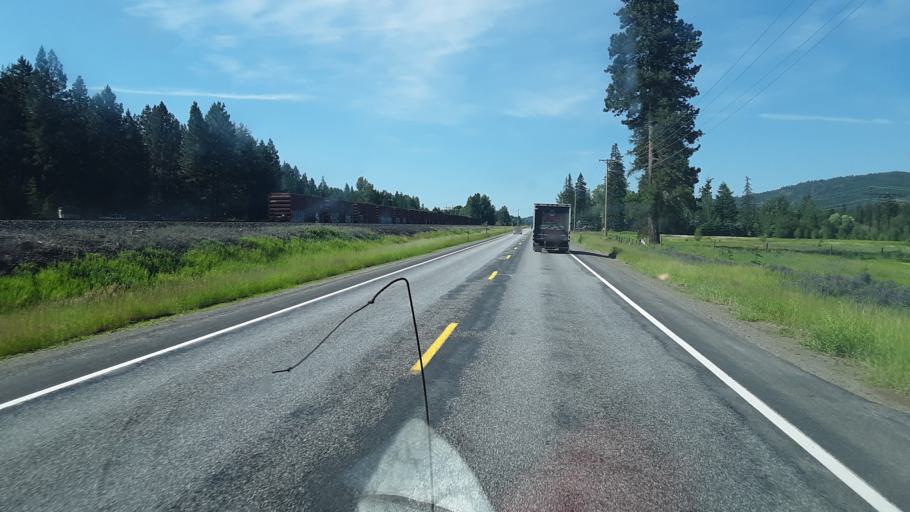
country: US
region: Idaho
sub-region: Bonner County
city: Ponderay
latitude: 48.4790
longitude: -116.4636
